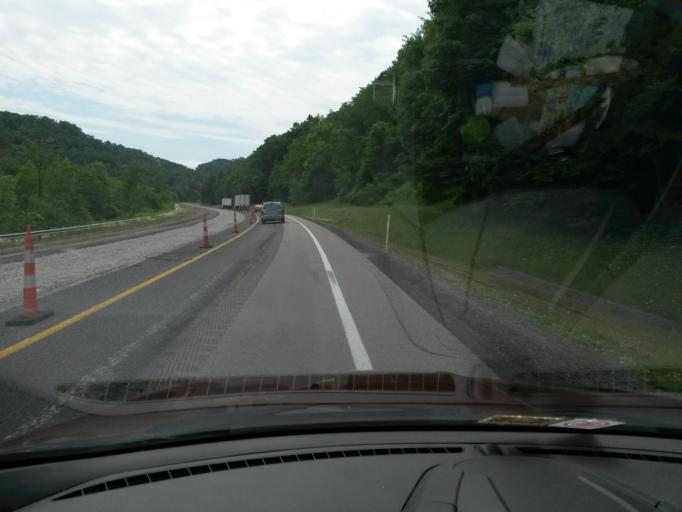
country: US
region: West Virginia
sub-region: Braxton County
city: Sutton
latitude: 38.7377
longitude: -80.6786
